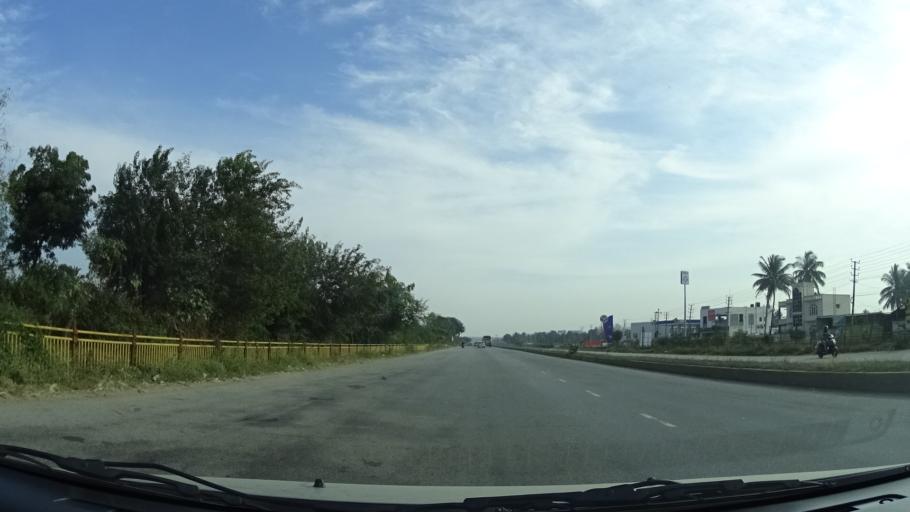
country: IN
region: Karnataka
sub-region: Bangalore Rural
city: Devanhalli
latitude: 13.2267
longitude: 77.6874
